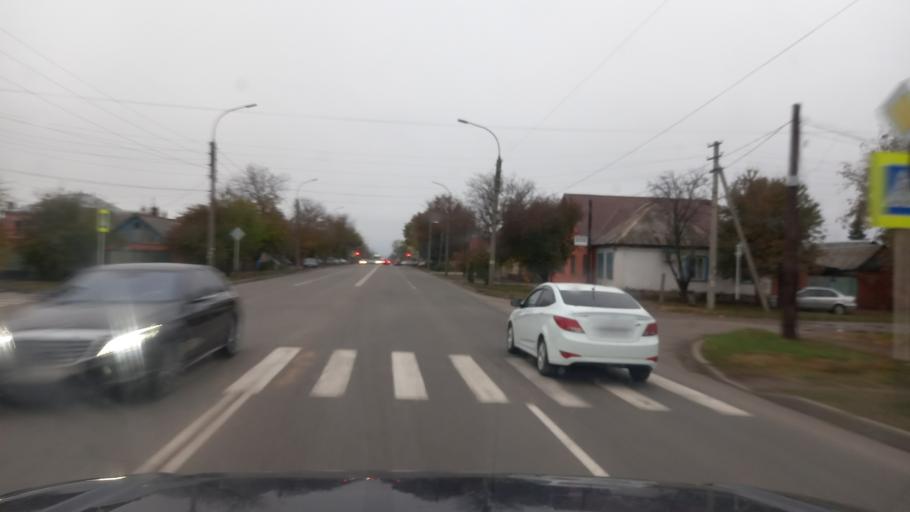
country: RU
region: Adygeya
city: Maykop
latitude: 44.6184
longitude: 40.0977
